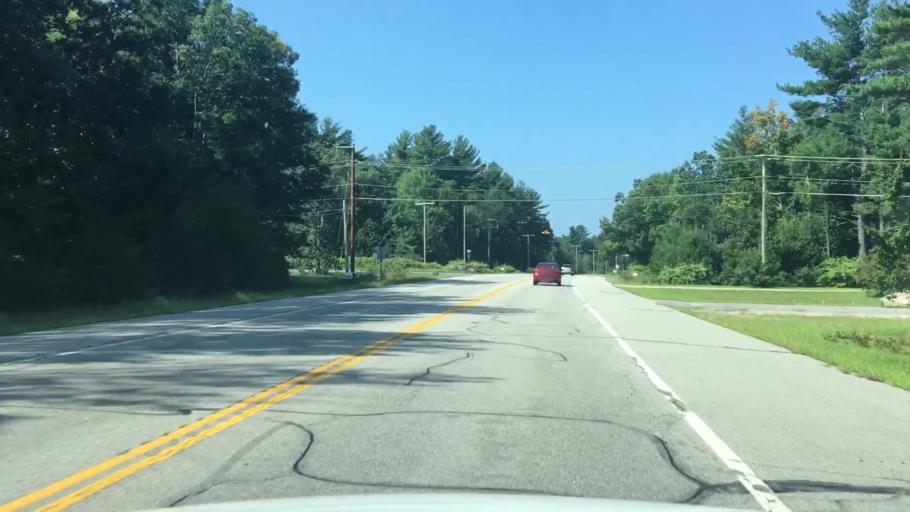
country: US
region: New Hampshire
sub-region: Rockingham County
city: Danville
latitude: 42.9091
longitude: -71.0855
